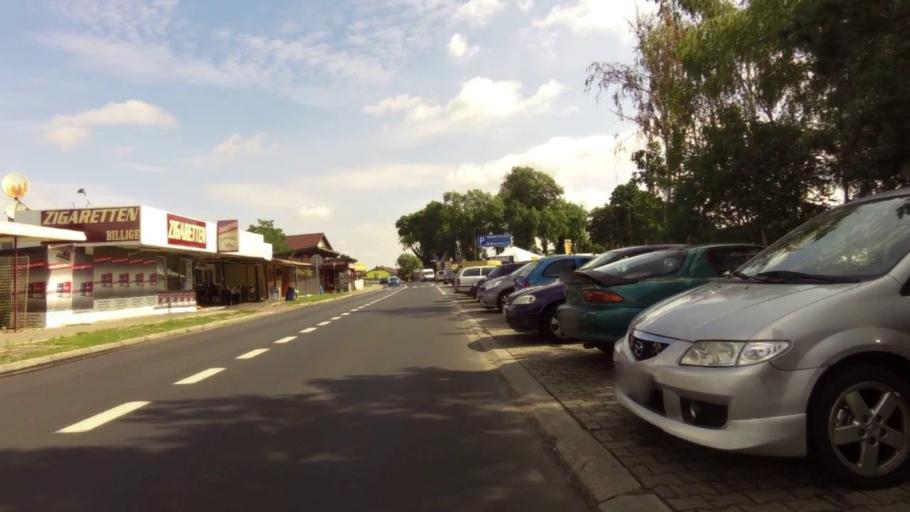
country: PL
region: West Pomeranian Voivodeship
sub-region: Powiat gryfinski
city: Cedynia
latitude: 52.8494
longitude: 14.1429
